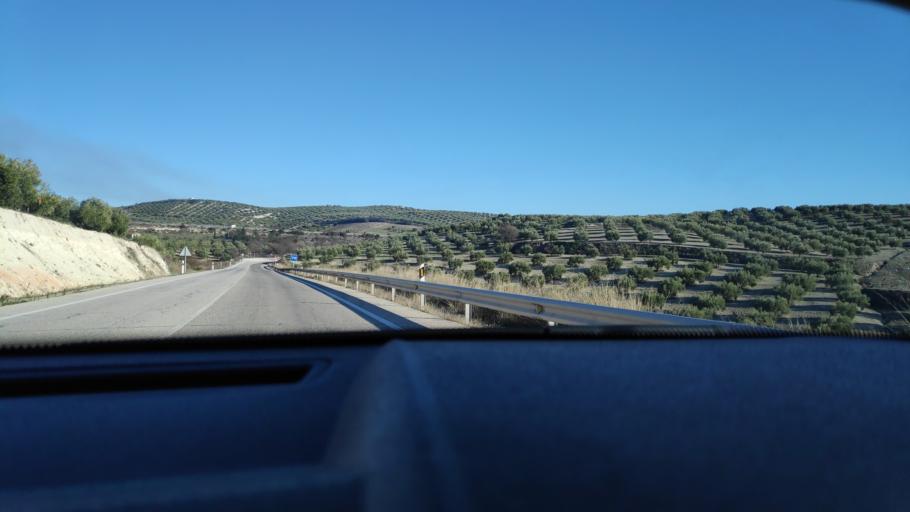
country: ES
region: Andalusia
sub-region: Province of Cordoba
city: Baena
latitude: 37.6005
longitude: -4.3110
